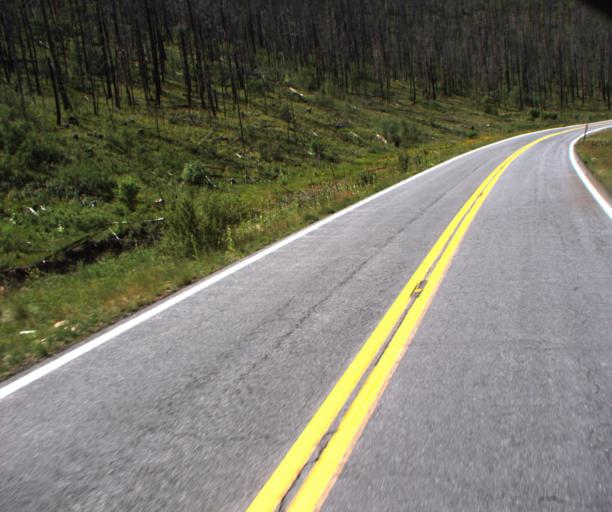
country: US
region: Arizona
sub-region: Apache County
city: Eagar
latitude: 33.7947
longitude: -109.1552
